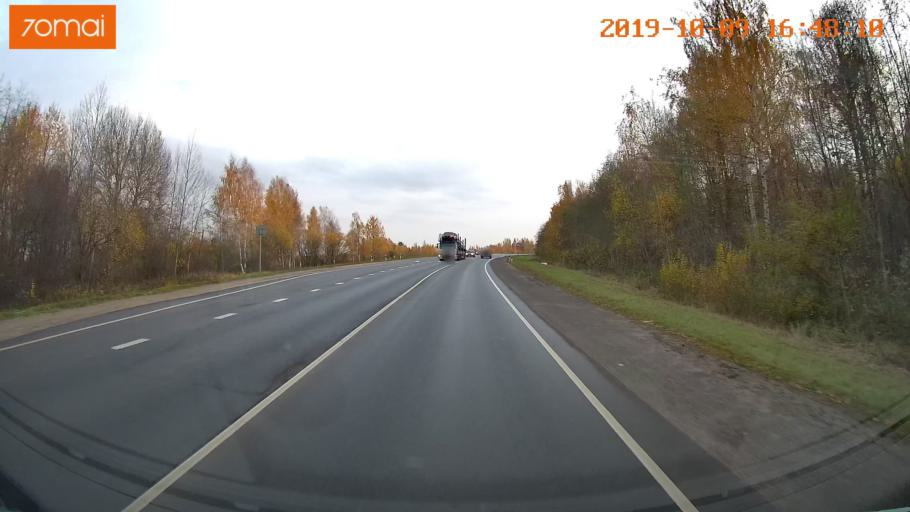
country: RU
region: Kostroma
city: Volgorechensk
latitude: 57.4306
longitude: 41.1891
